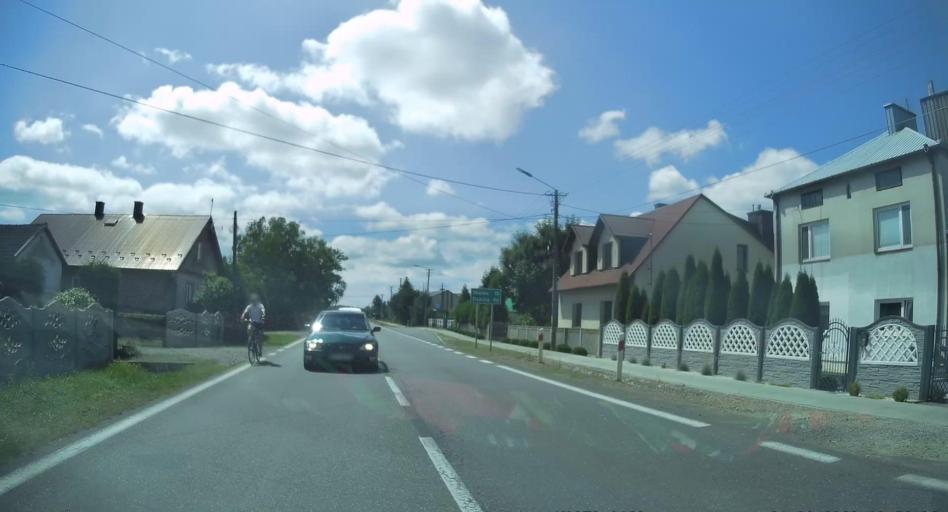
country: PL
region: Subcarpathian Voivodeship
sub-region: Powiat mielecki
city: Padew Narodowa
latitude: 50.4177
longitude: 21.4809
